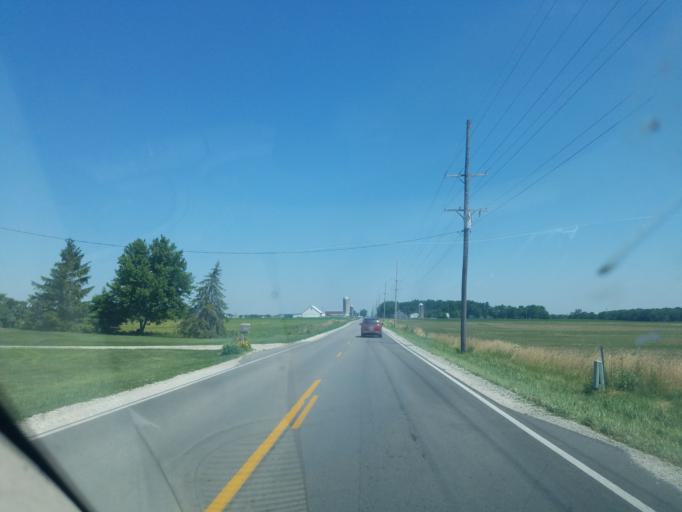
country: US
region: Ohio
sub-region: Mercer County
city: Saint Henry
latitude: 40.4300
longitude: -84.6483
